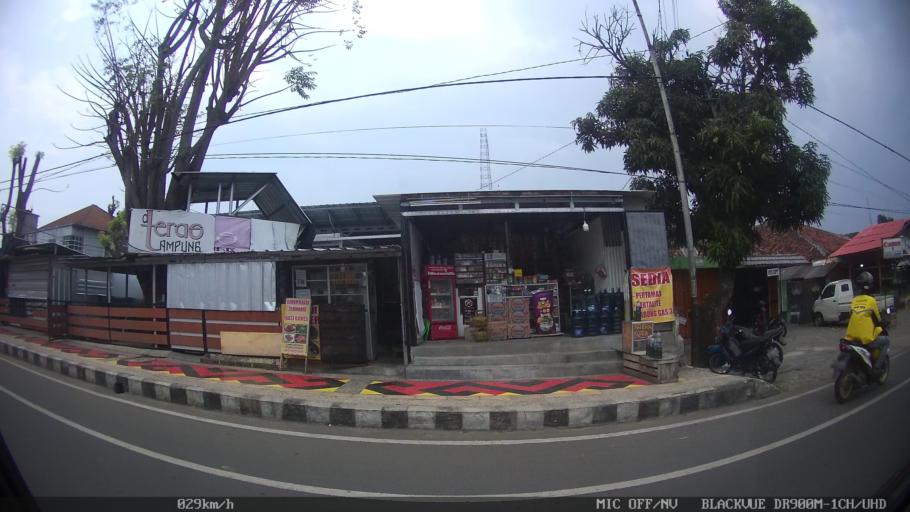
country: ID
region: Lampung
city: Bandarlampung
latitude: -5.4286
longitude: 105.2699
